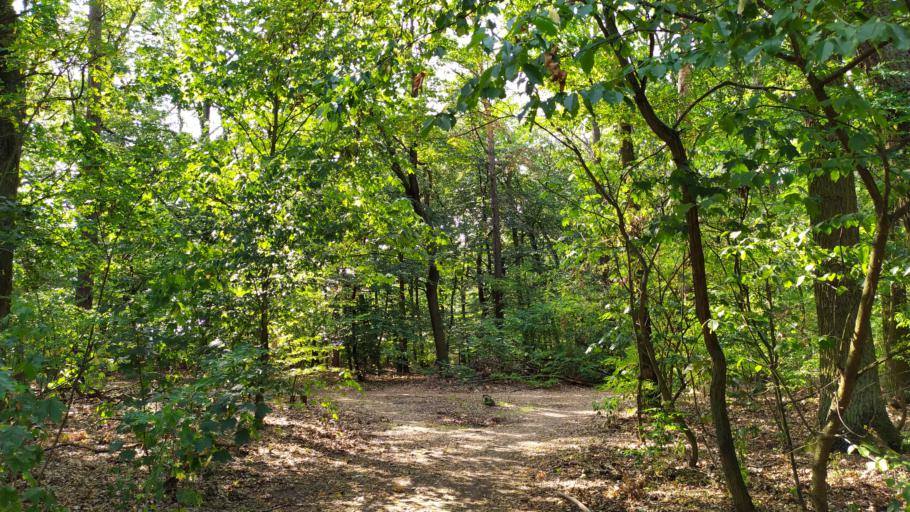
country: DE
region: Berlin
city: Grunau
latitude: 52.4157
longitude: 13.6020
